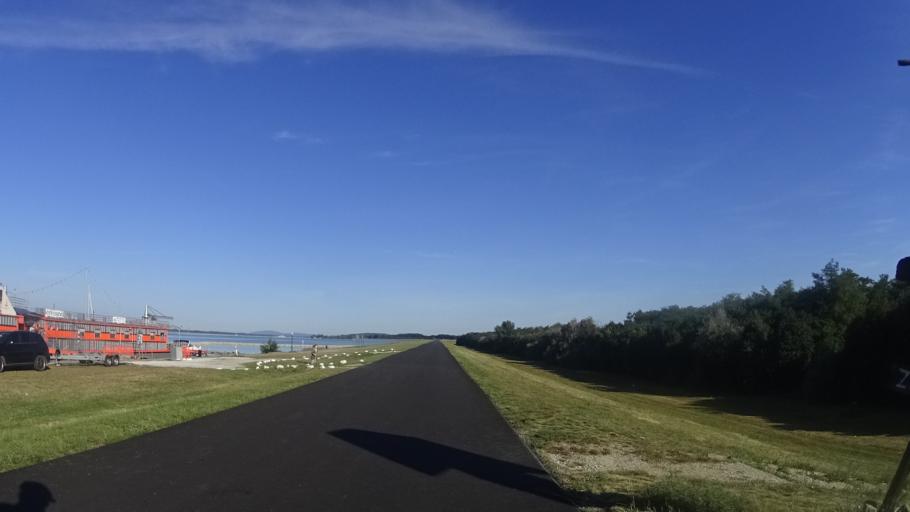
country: SK
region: Trnavsky
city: Samorin
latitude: 48.0090
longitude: 17.3048
